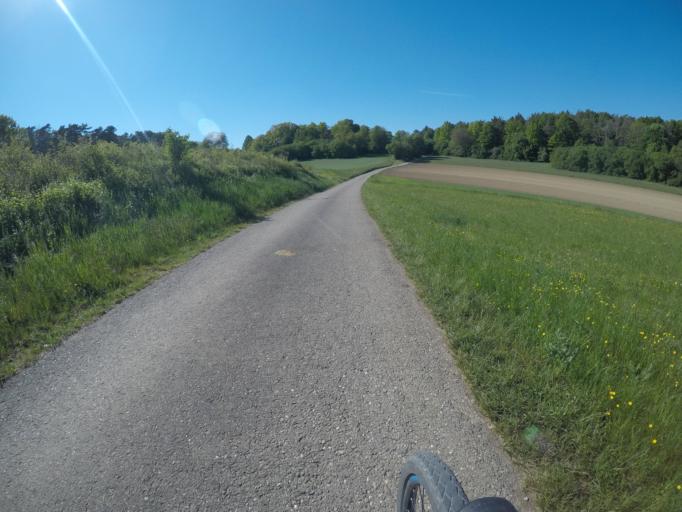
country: DE
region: Baden-Wuerttemberg
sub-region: Karlsruhe Region
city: Friolzheim
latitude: 48.8233
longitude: 8.8501
